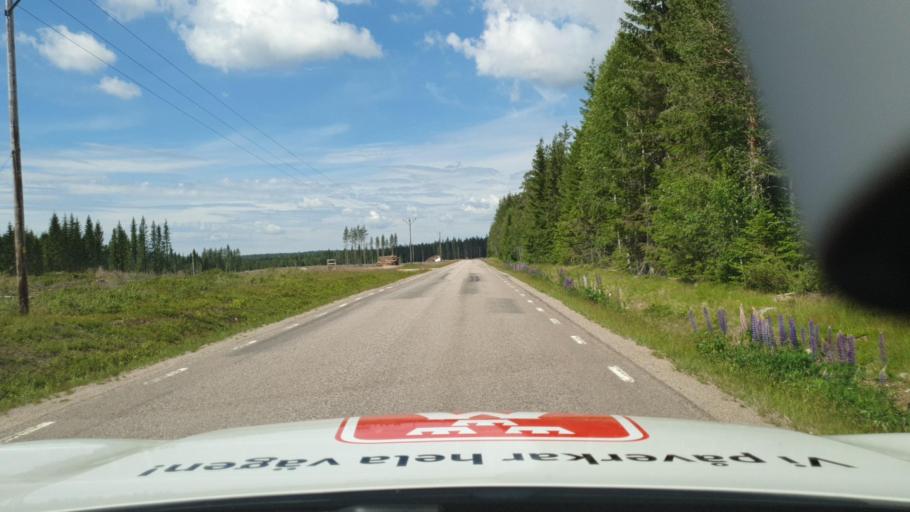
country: SE
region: Vaermland
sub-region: Torsby Kommun
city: Torsby
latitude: 60.4964
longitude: 12.8637
